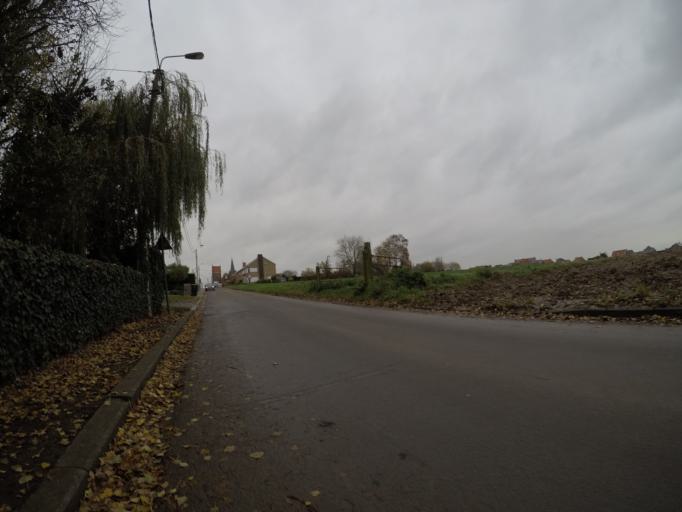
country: BE
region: Flanders
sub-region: Provincie West-Vlaanderen
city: Saint-Yvon
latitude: 50.7830
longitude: 2.8836
